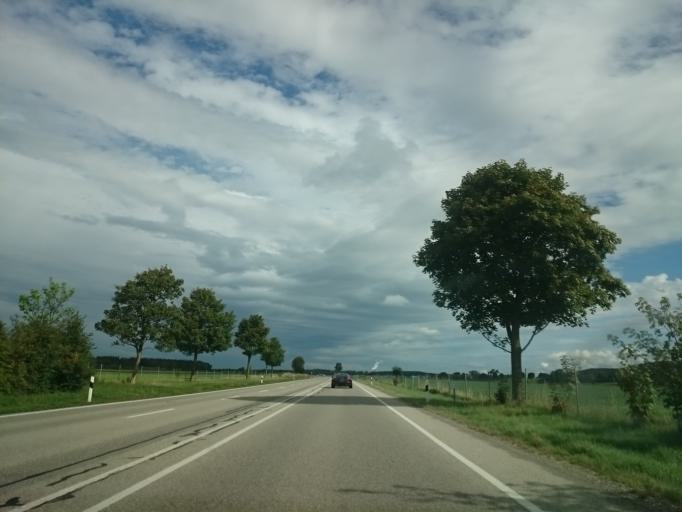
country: DE
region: Bavaria
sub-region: Swabia
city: Rieden
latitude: 47.9506
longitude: 10.6755
